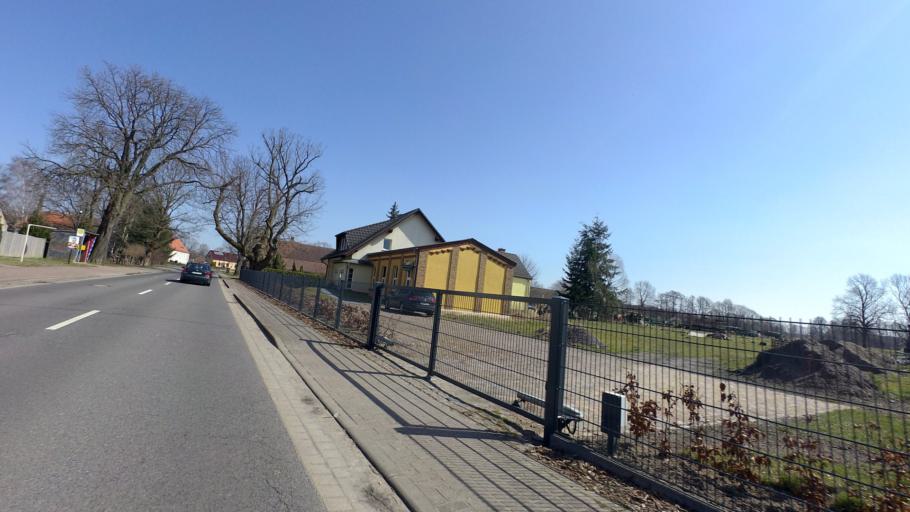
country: DE
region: Brandenburg
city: Lindow
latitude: 52.9318
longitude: 12.9693
